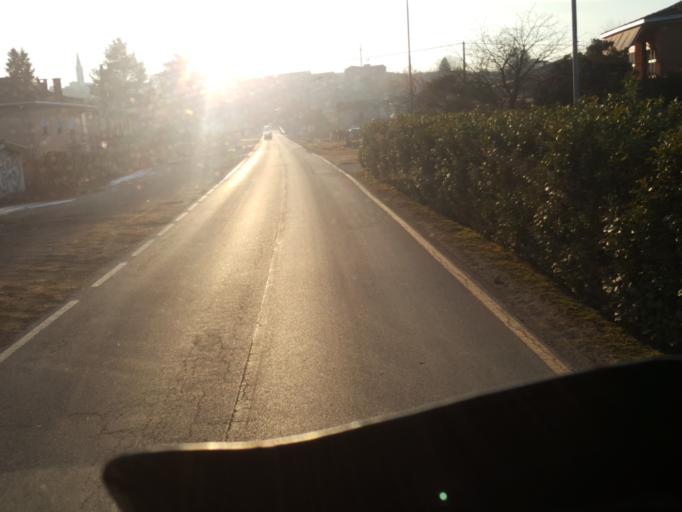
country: IT
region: Piedmont
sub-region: Provincia di Novara
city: Borgo Ticino
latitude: 45.6926
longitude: 8.6089
